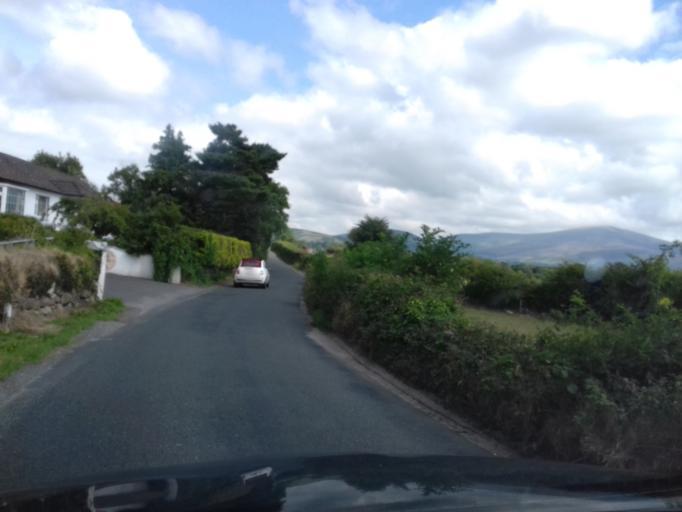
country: IE
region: Leinster
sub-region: Kilkenny
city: Graiguenamanagh
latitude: 52.6011
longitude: -6.9109
